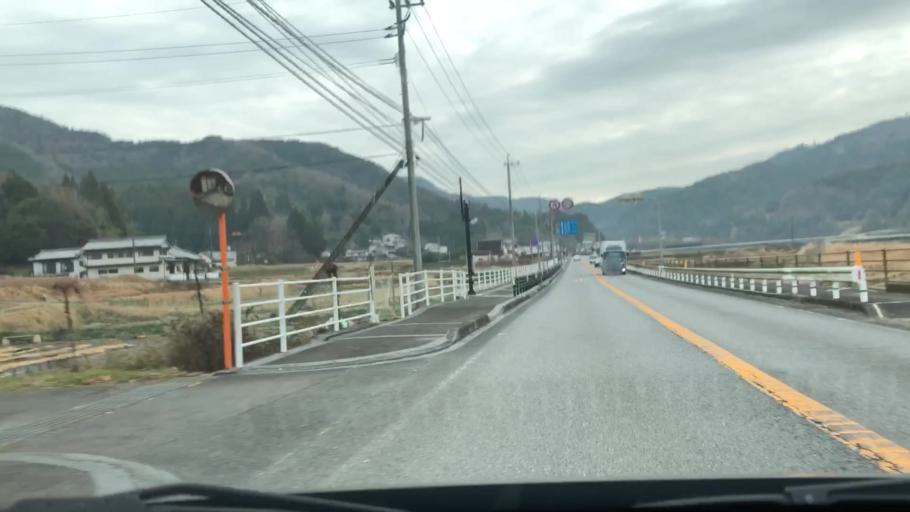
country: JP
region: Oita
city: Usuki
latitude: 33.0063
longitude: 131.7195
